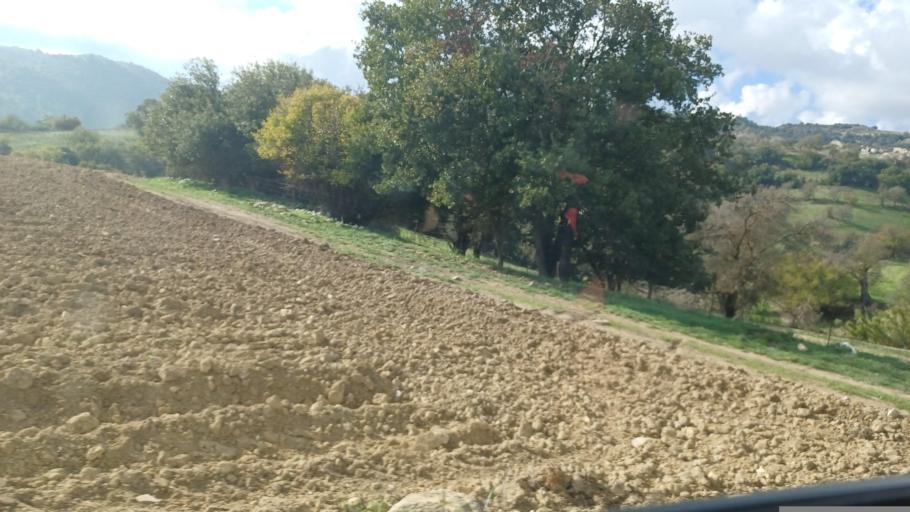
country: CY
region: Pafos
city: Mesogi
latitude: 34.8395
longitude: 32.5385
